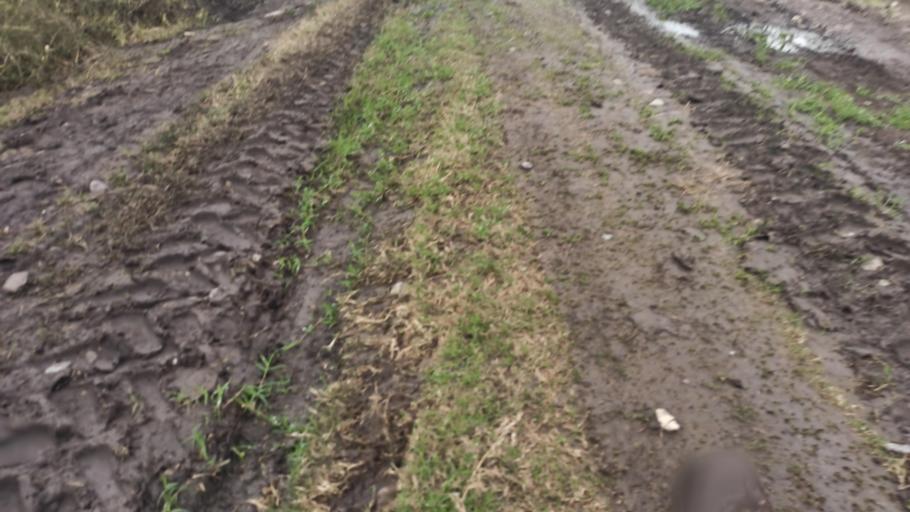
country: MX
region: Puebla
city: Espinal
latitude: 20.3058
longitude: -97.4125
